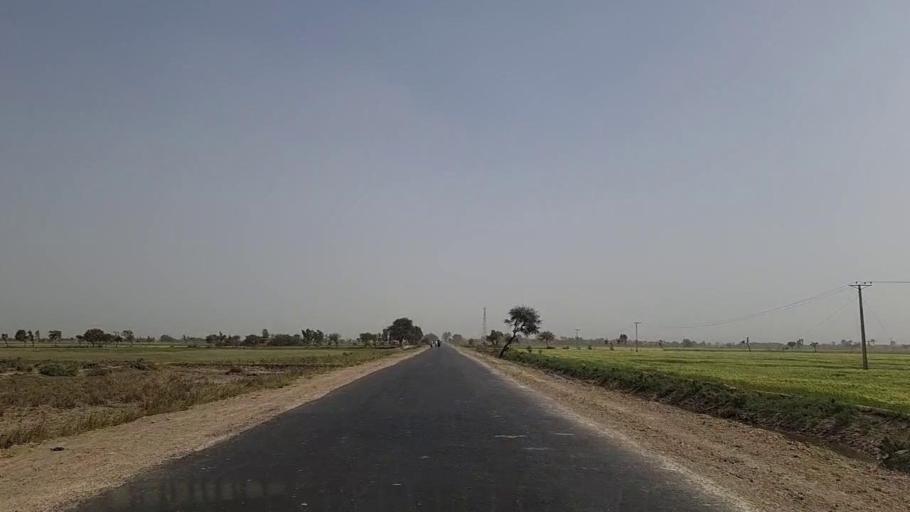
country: PK
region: Sindh
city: Tando Bago
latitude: 24.8216
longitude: 68.9021
